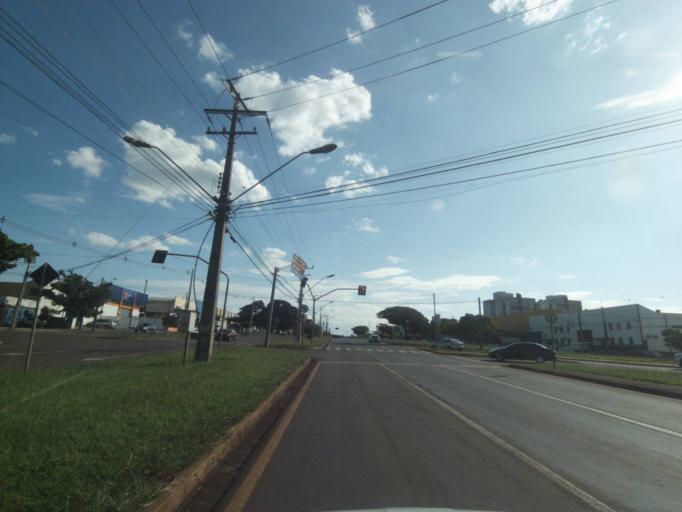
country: BR
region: Parana
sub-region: Londrina
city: Londrina
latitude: -23.3511
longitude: -51.1471
